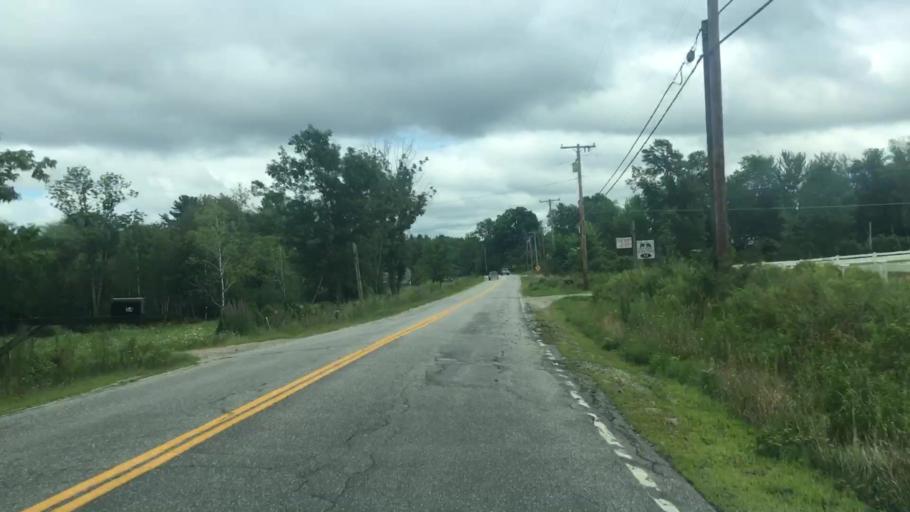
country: US
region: Maine
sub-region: York County
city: Limerick
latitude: 43.6762
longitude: -70.7835
